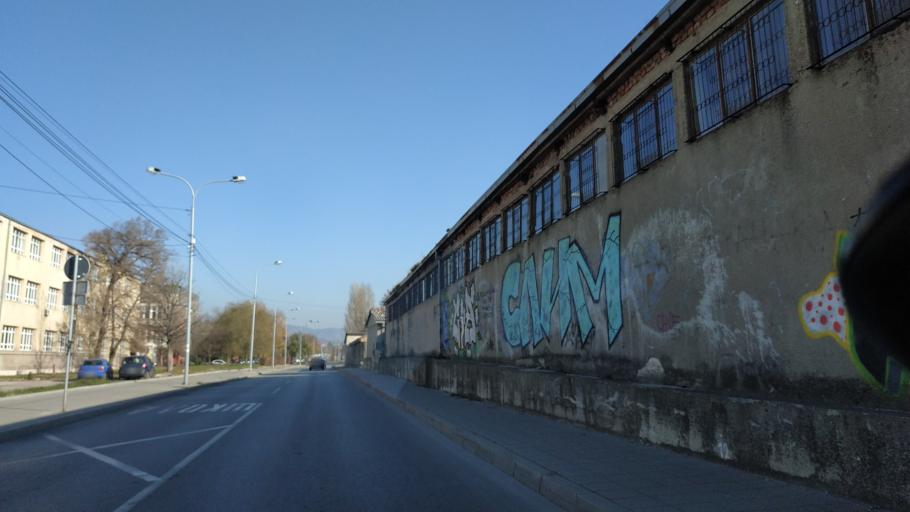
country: RS
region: Central Serbia
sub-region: Nisavski Okrug
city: Nis
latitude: 43.3288
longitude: 21.8891
